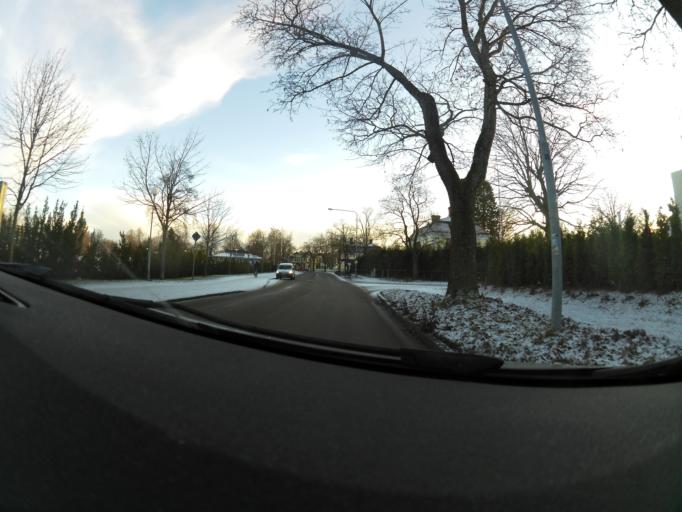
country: SE
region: Gaevleborg
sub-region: Gavle Kommun
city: Gavle
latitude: 60.6718
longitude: 17.1313
